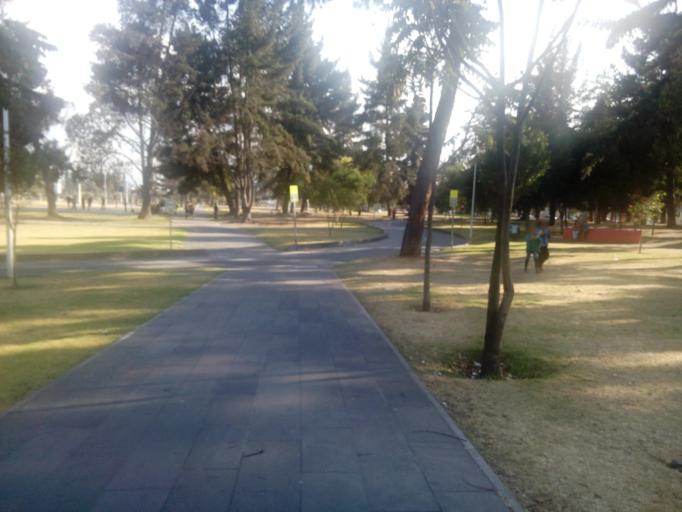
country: EC
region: Pichincha
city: Quito
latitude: -0.1769
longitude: -78.4831
